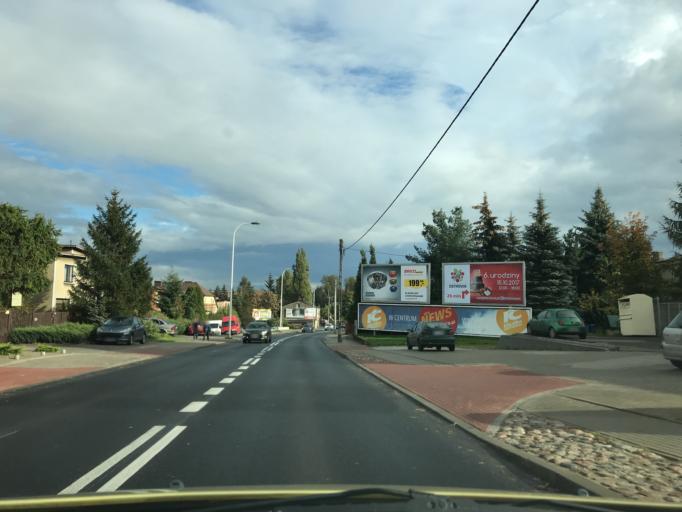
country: PL
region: Greater Poland Voivodeship
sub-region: Kalisz
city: Kalisz
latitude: 51.7620
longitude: 18.0687
